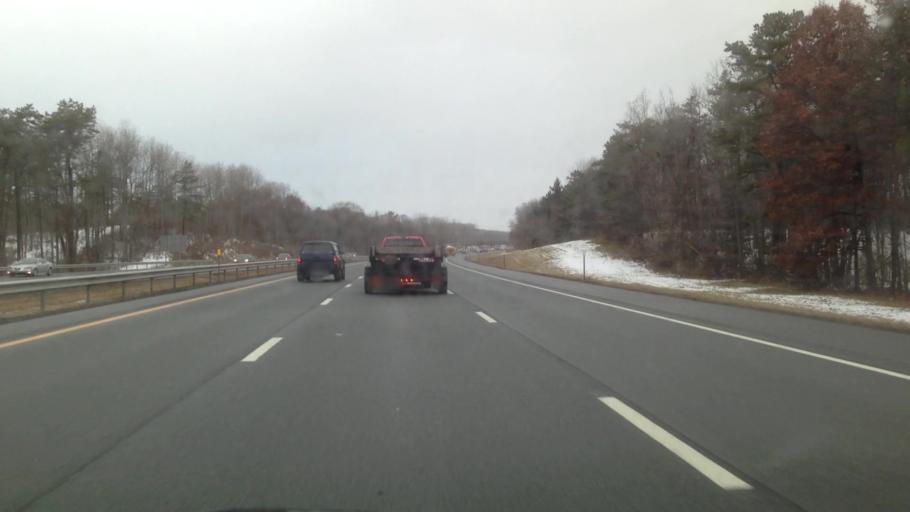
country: US
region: New York
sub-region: Albany County
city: Westmere
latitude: 42.7210
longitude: -73.8815
